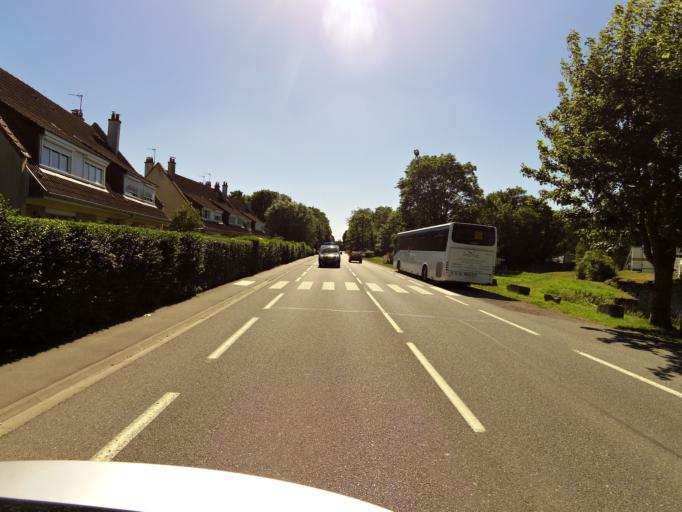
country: FR
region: Nord-Pas-de-Calais
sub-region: Departement du Nord
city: Bergues
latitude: 50.9725
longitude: 2.4360
